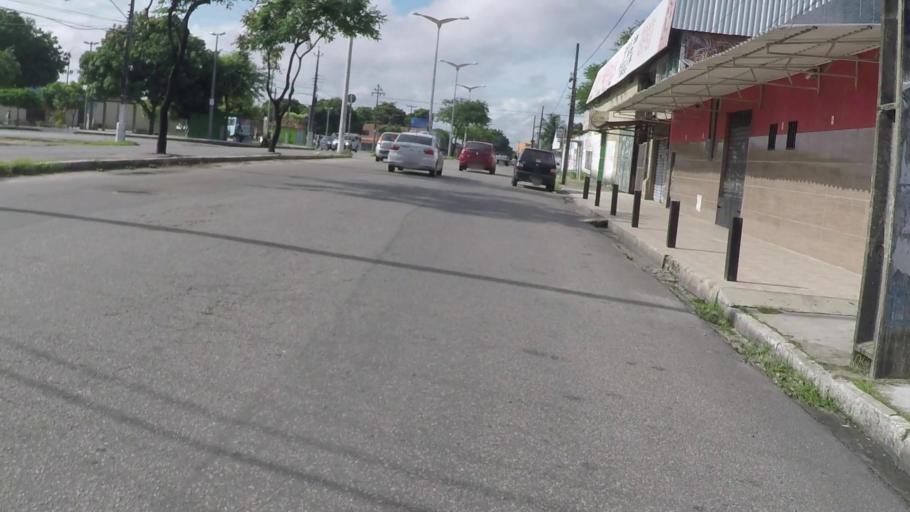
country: BR
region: Ceara
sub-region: Fortaleza
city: Fortaleza
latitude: -3.7082
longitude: -38.5904
